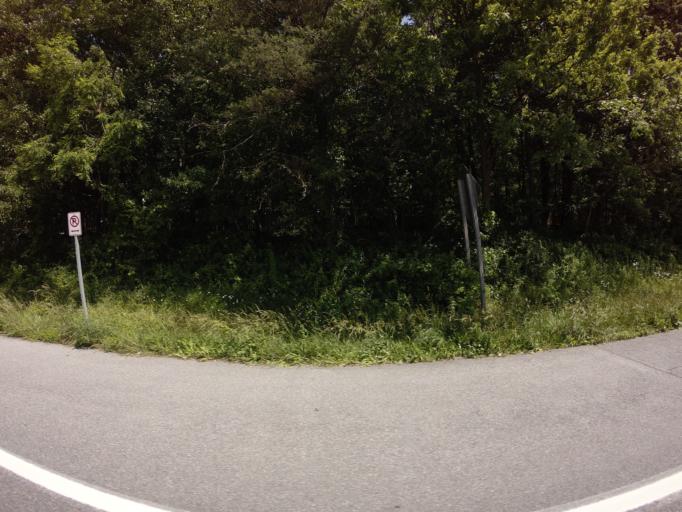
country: US
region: Maryland
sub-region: Carroll County
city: Eldersburg
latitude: 39.3985
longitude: -76.9545
